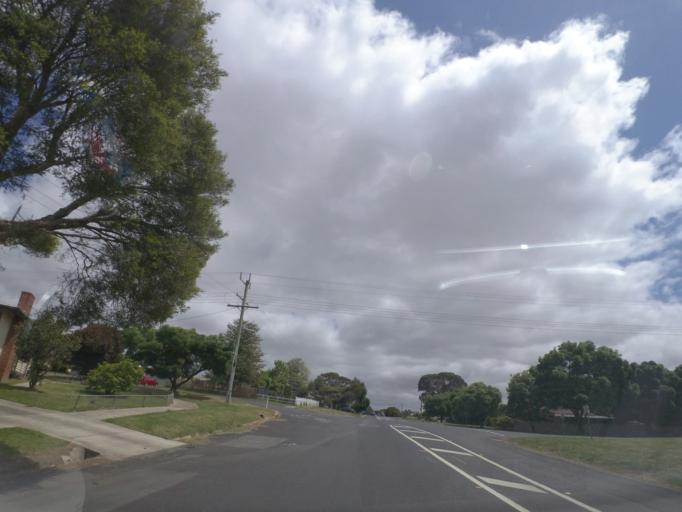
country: AU
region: Victoria
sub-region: Whittlesea
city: Whittlesea
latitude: -37.2100
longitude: 145.0461
